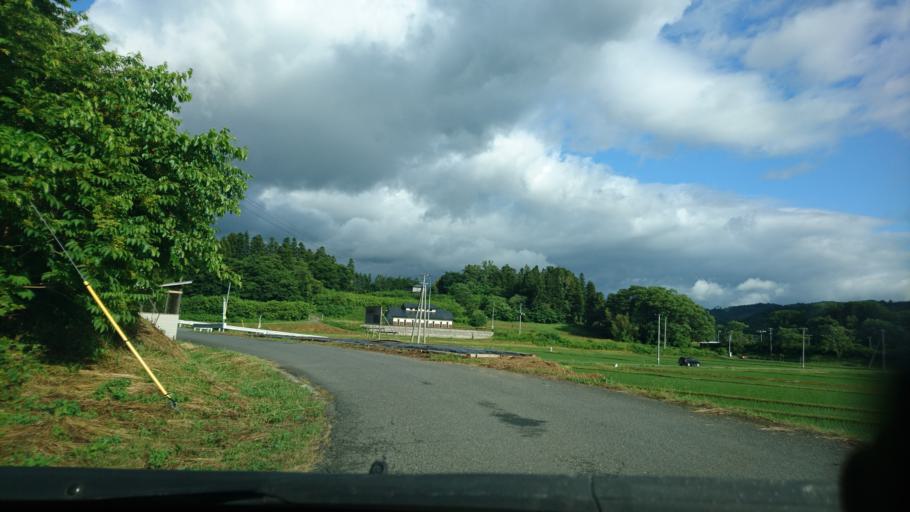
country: JP
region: Iwate
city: Ichinoseki
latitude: 38.8546
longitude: 141.2877
